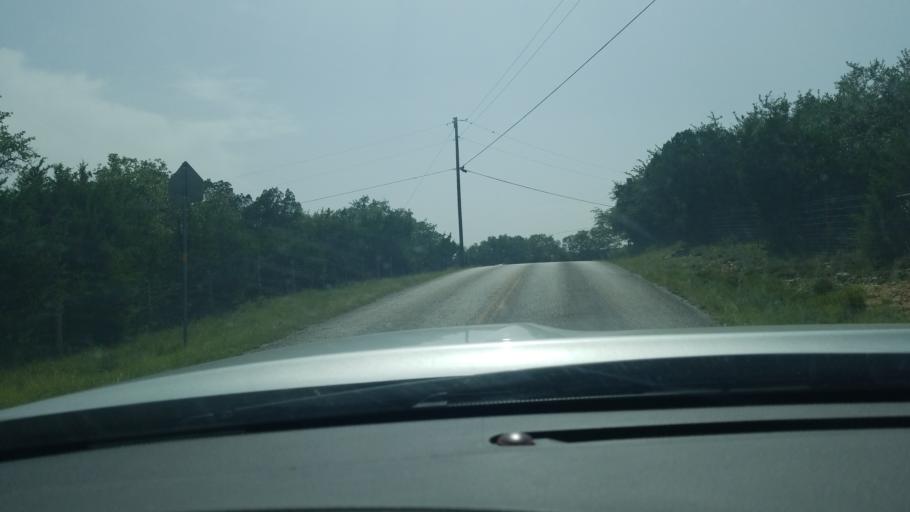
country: US
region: Texas
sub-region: Comal County
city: Bulverde
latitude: 29.7931
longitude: -98.4350
